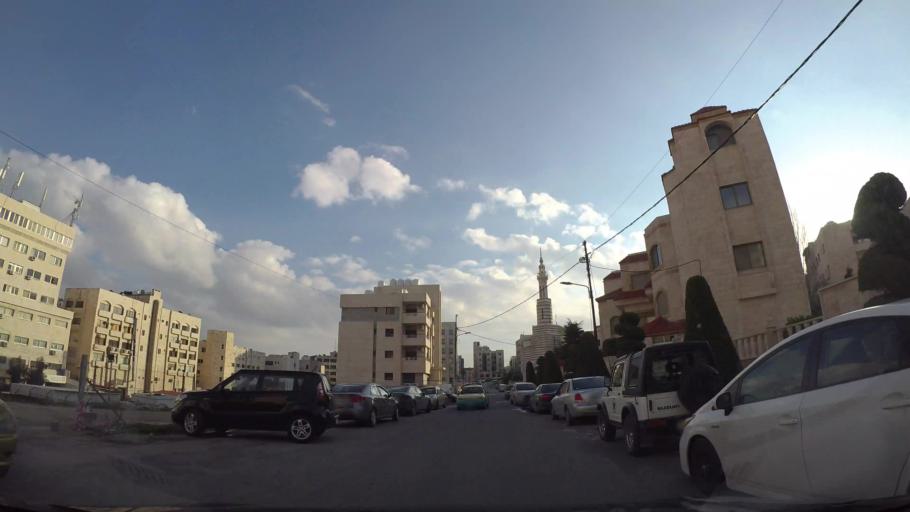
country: JO
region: Amman
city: Al Jubayhah
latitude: 31.9760
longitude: 35.8864
